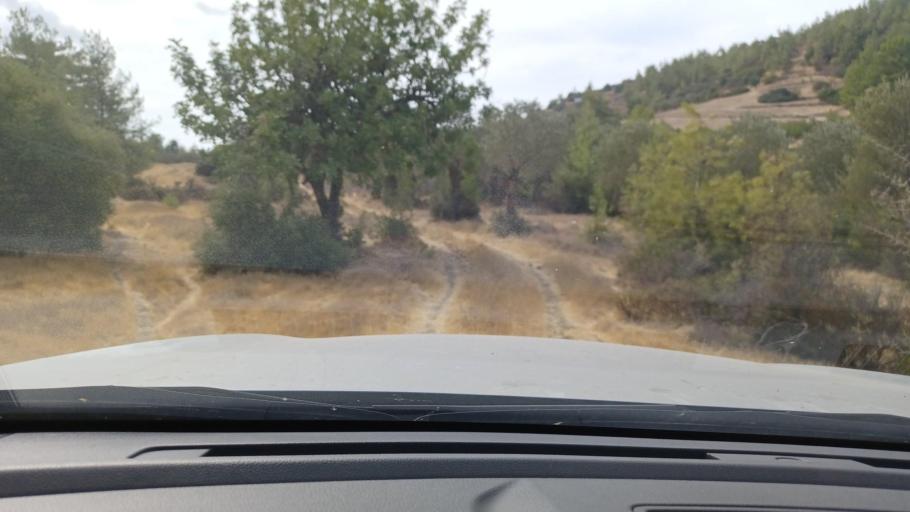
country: CY
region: Pafos
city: Polis
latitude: 35.0076
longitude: 32.5398
